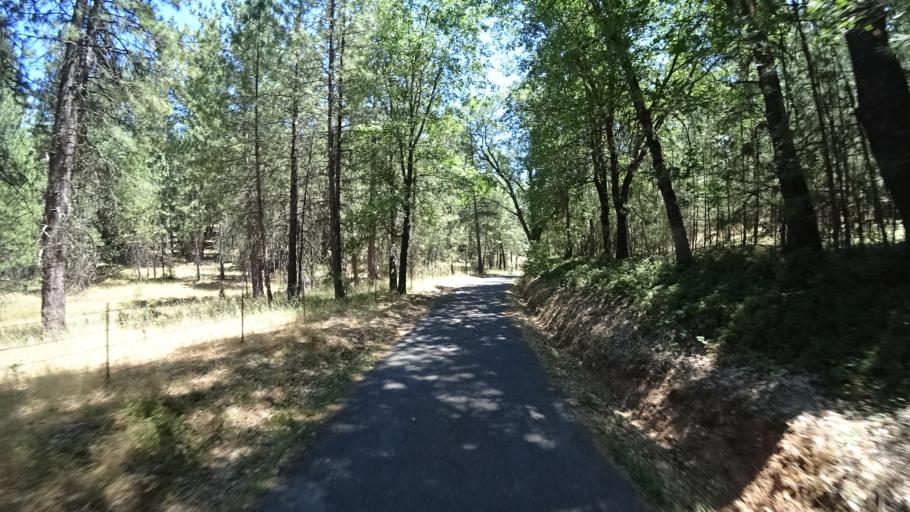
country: US
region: California
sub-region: Calaveras County
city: Mountain Ranch
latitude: 38.3291
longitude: -120.5089
